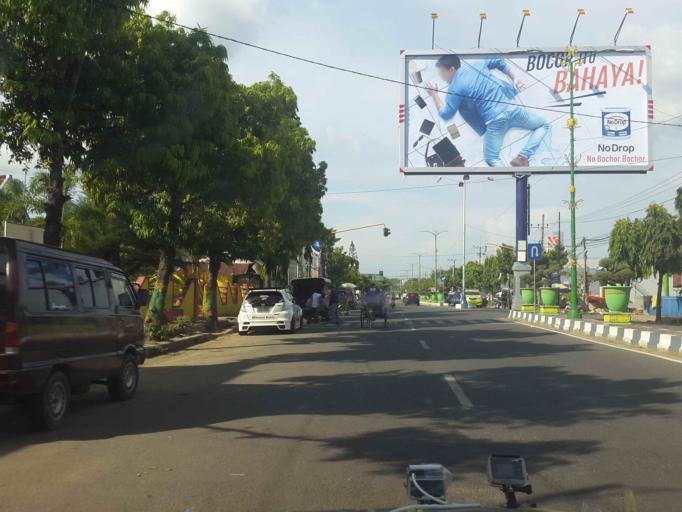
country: ID
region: East Java
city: Sumenep
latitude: -7.0168
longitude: 113.8579
